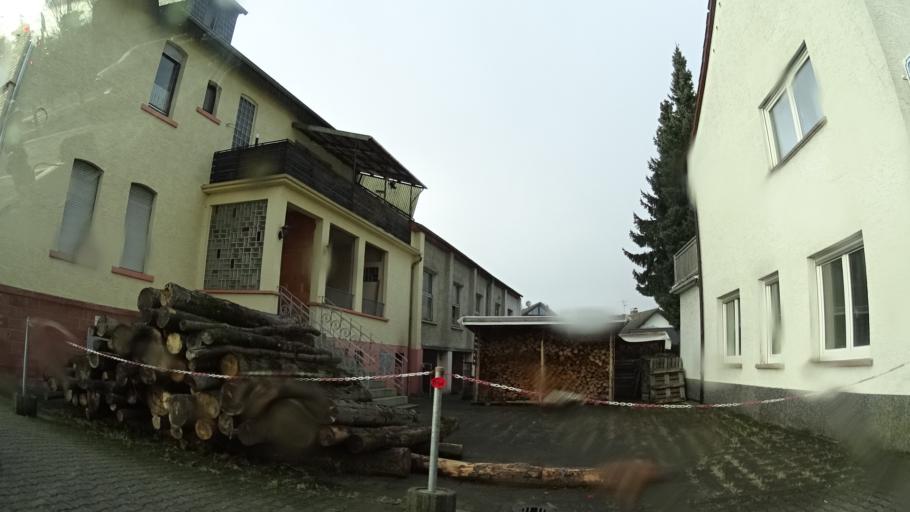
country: DE
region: Hesse
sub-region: Regierungsbezirk Darmstadt
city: Langenselbold
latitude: 50.1612
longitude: 9.0909
